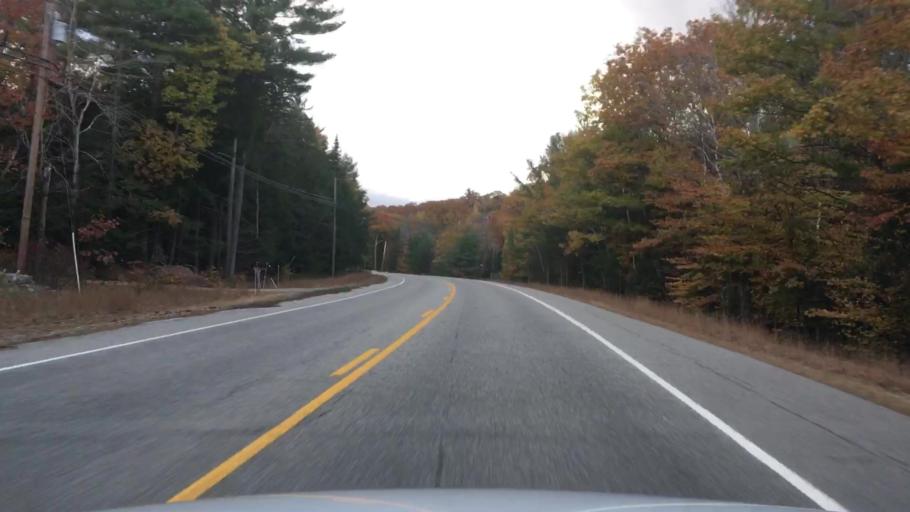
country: US
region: Maine
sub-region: Androscoggin County
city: Livermore
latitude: 44.3969
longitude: -70.2572
